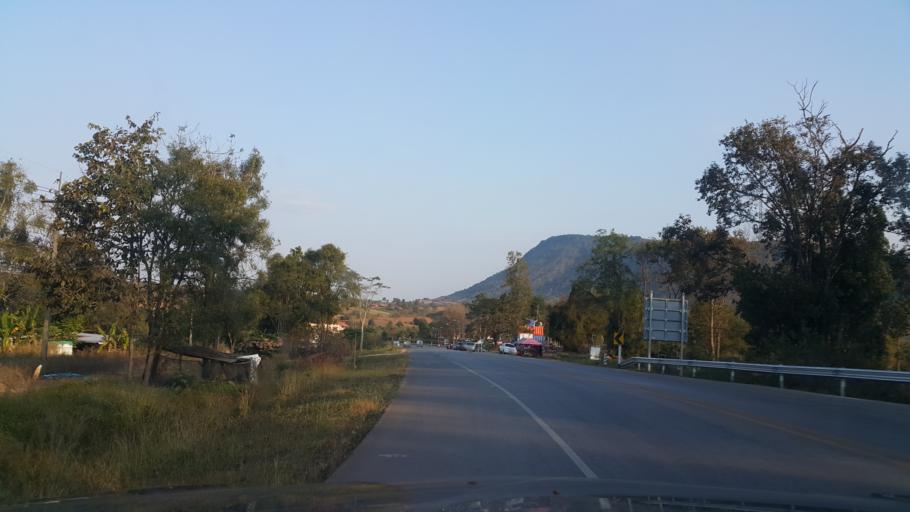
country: TH
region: Loei
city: Phu Ruea
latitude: 17.4578
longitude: 101.5056
